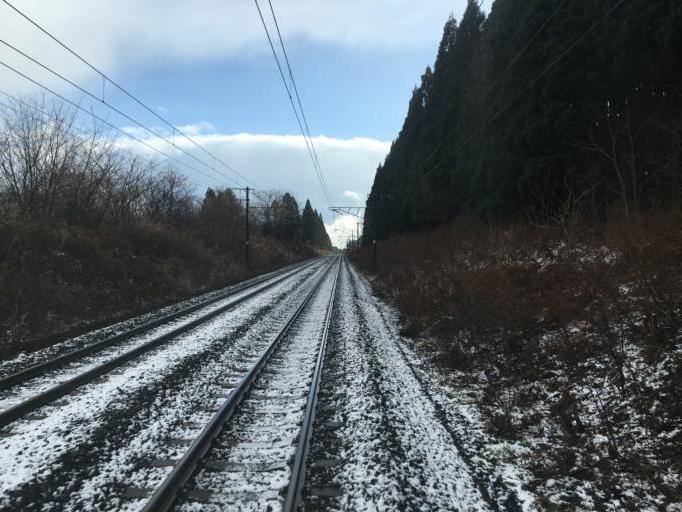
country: JP
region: Aomori
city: Aomori Shi
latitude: 40.9108
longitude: 141.0489
